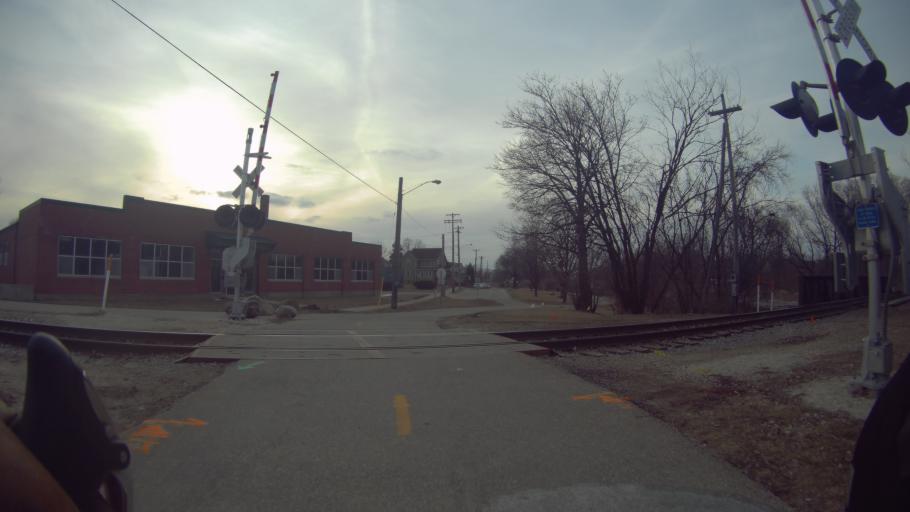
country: US
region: Wisconsin
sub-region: Dane County
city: Maple Bluff
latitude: 43.0909
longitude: -89.3636
